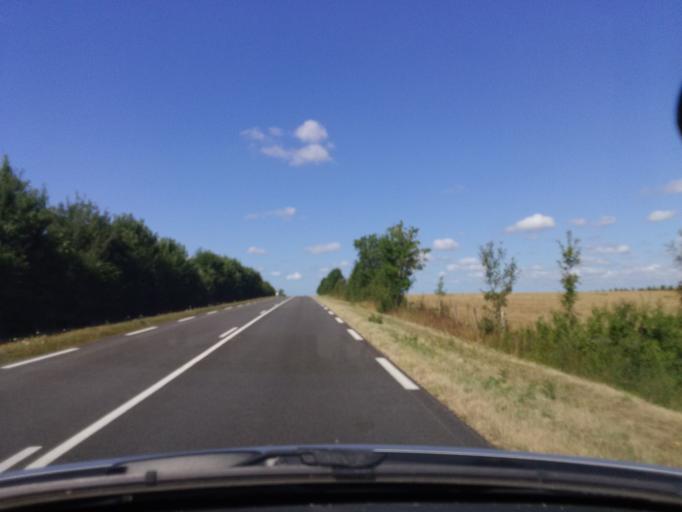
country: FR
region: Pays de la Loire
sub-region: Departement de la Vendee
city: Le Champ-Saint-Pere
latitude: 46.4577
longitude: -1.3655
